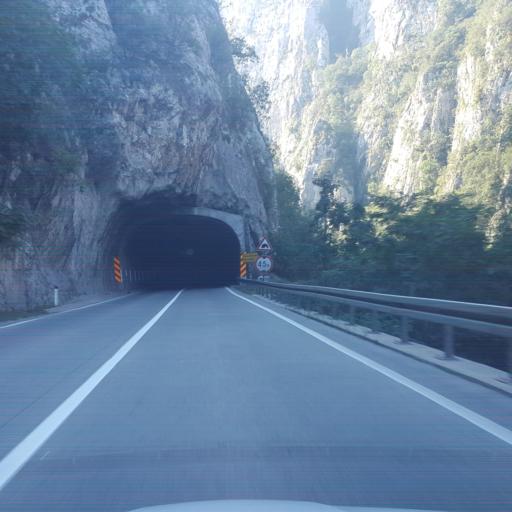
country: RS
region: Central Serbia
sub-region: Nisavski Okrug
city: Svrljig
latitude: 43.3196
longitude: 22.1731
